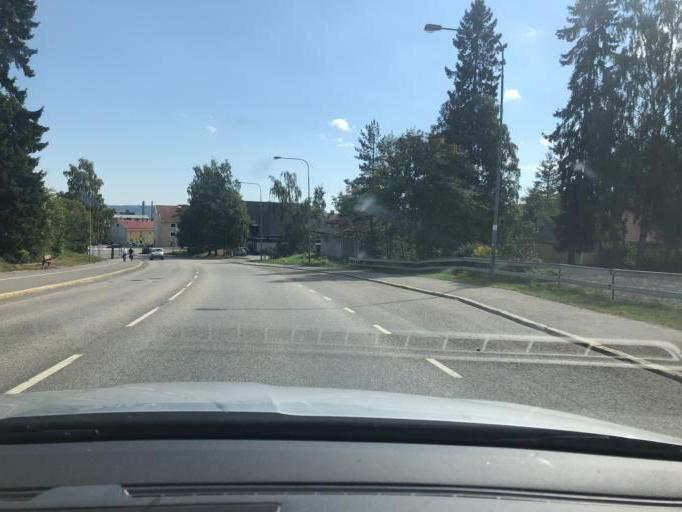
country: SE
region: Vaesternorrland
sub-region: Sundsvalls Kommun
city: Sundsvall
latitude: 62.4014
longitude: 17.3246
